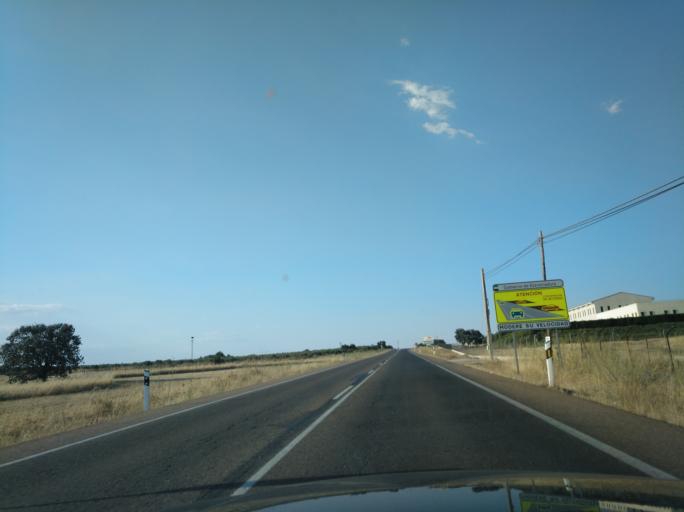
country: ES
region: Extremadura
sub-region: Provincia de Badajoz
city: Olivenza
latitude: 38.7075
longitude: -7.0865
